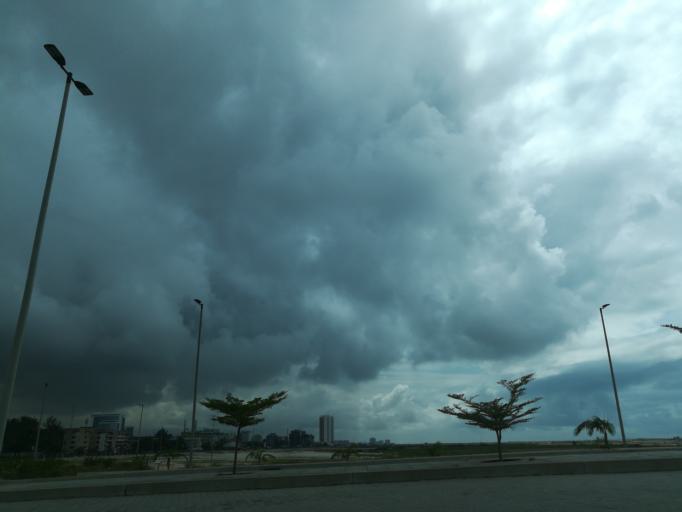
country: NG
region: Lagos
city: Lagos
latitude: 6.4208
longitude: 3.4135
